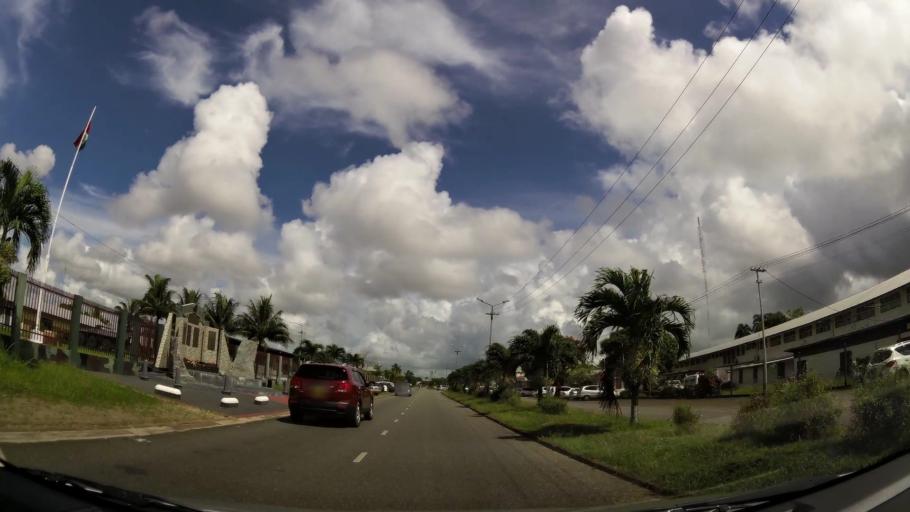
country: SR
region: Paramaribo
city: Paramaribo
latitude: 5.8280
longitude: -55.1780
